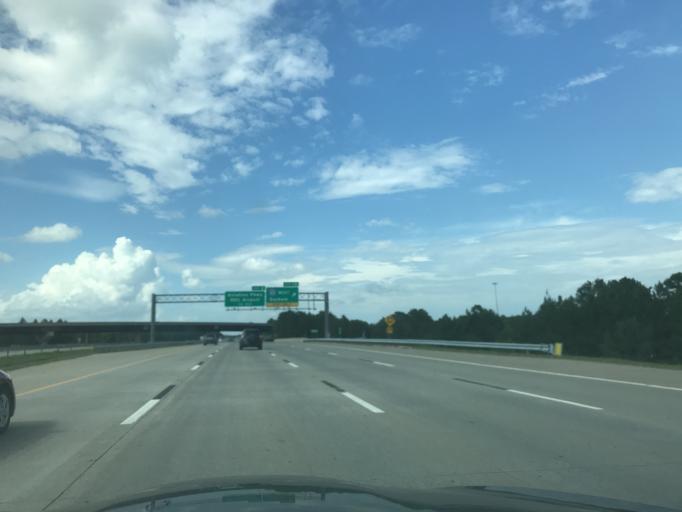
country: US
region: North Carolina
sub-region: Wake County
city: Morrisville
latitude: 35.8712
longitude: -78.8320
